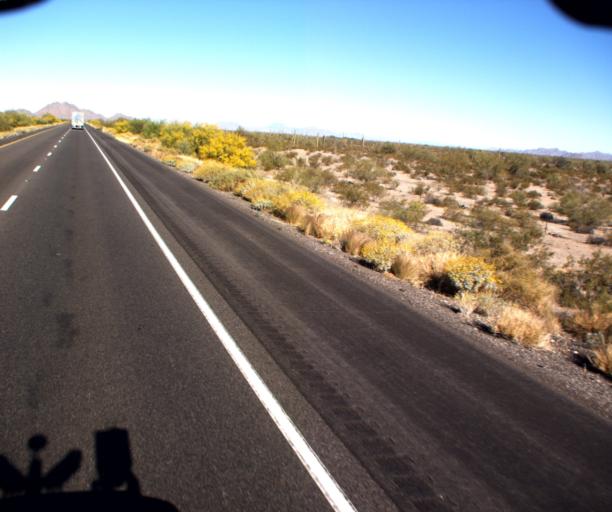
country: US
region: Arizona
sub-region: Maricopa County
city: Gila Bend
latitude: 32.8871
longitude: -112.4729
